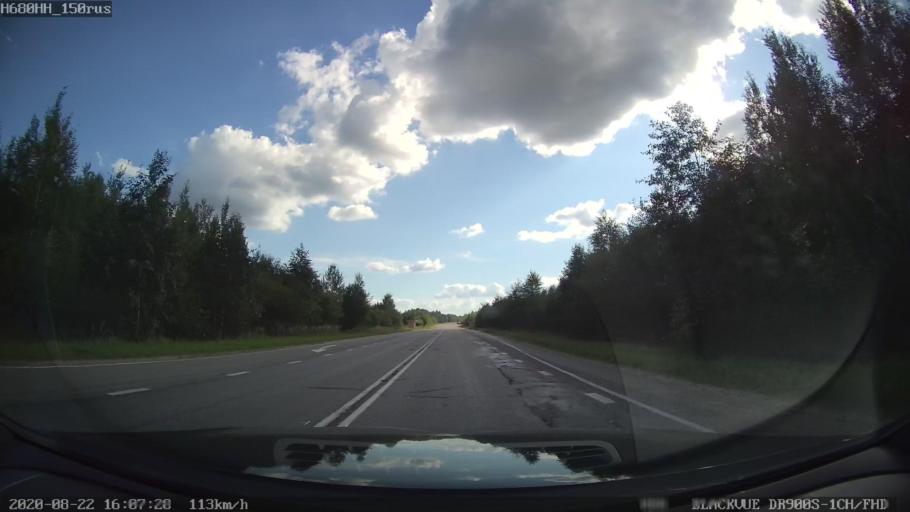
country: RU
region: Tverskaya
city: Rameshki
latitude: 57.5524
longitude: 36.3128
